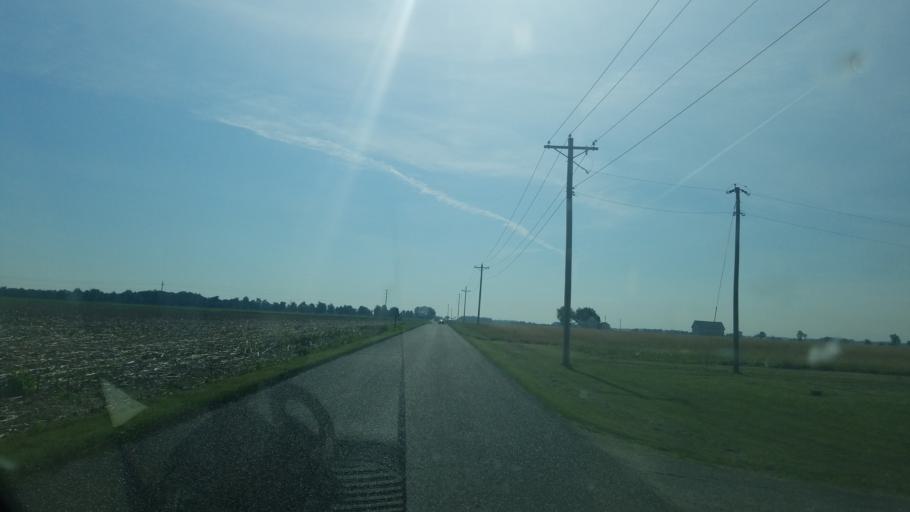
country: US
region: Ohio
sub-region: Hancock County
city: Findlay
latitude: 41.0214
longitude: -83.5483
